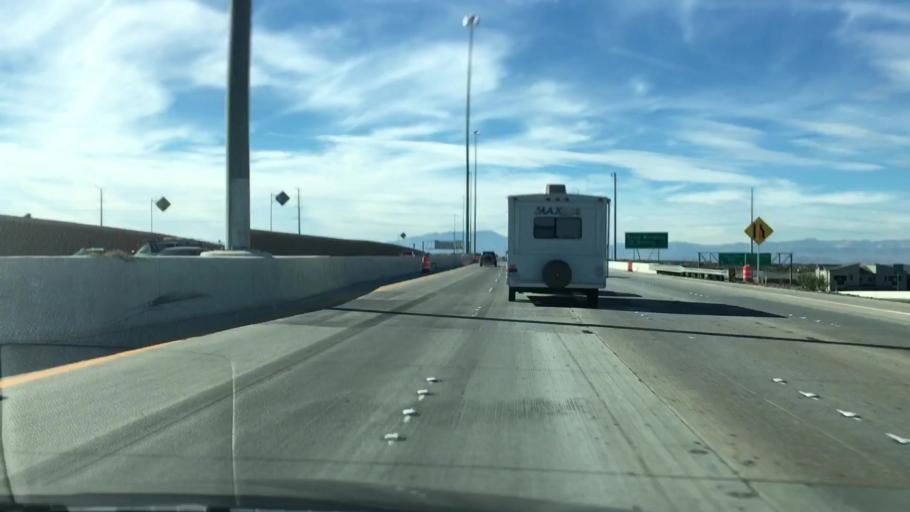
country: US
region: Nevada
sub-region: Clark County
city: Henderson
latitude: 36.0325
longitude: -115.0260
